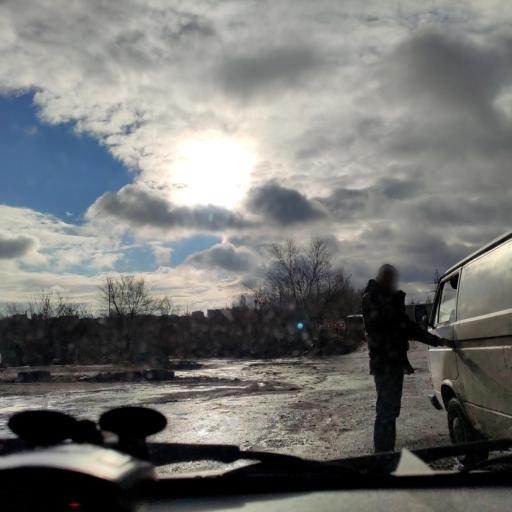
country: RU
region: Voronezj
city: Voronezh
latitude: 51.6889
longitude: 39.1444
